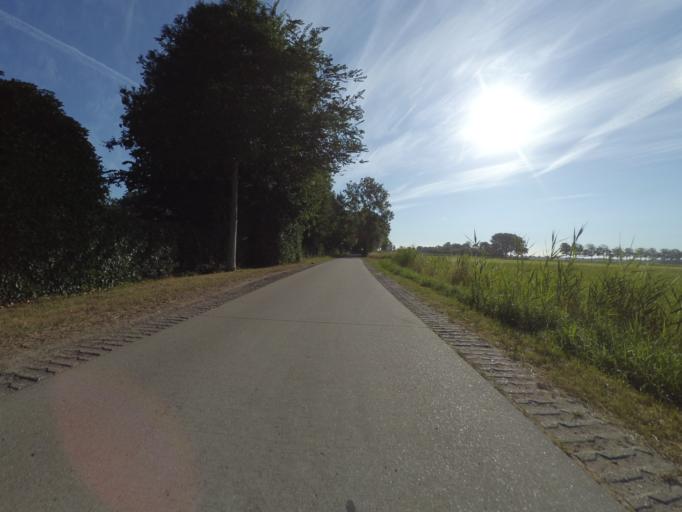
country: NL
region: Flevoland
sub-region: Gemeente Dronten
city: Biddinghuizen
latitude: 52.3817
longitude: 5.7062
